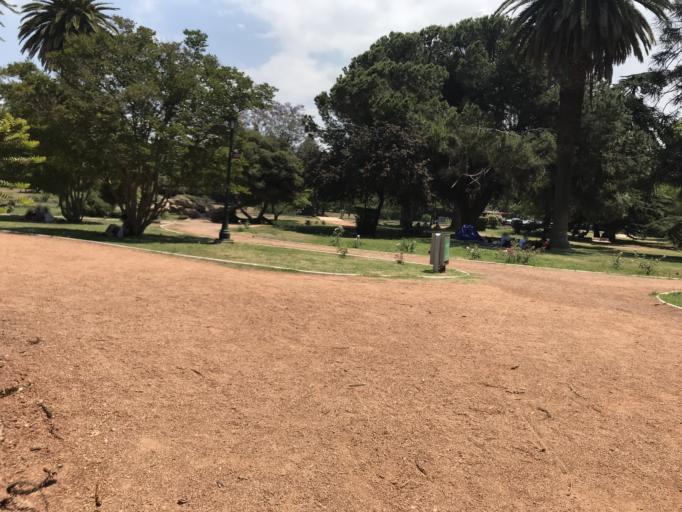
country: AR
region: Mendoza
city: Mendoza
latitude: -32.8902
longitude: -68.8668
